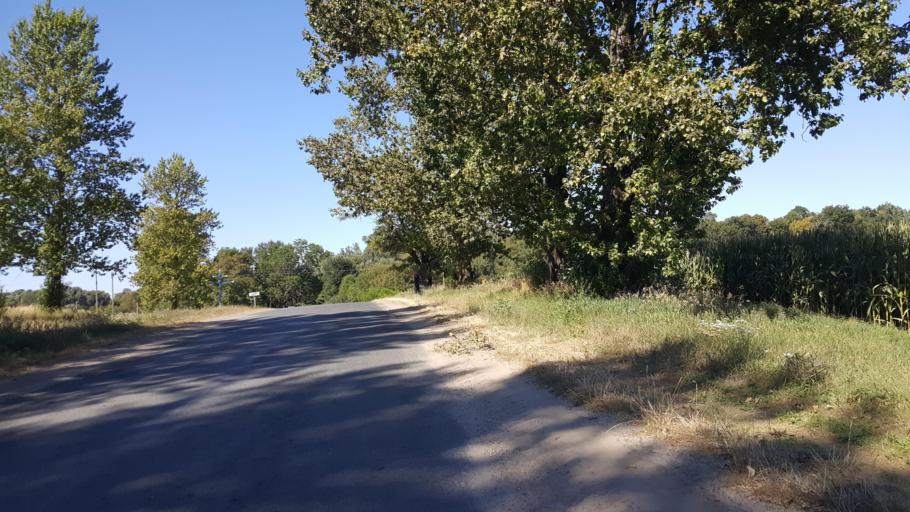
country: BY
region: Brest
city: Vysokaye
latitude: 52.2183
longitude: 23.4574
